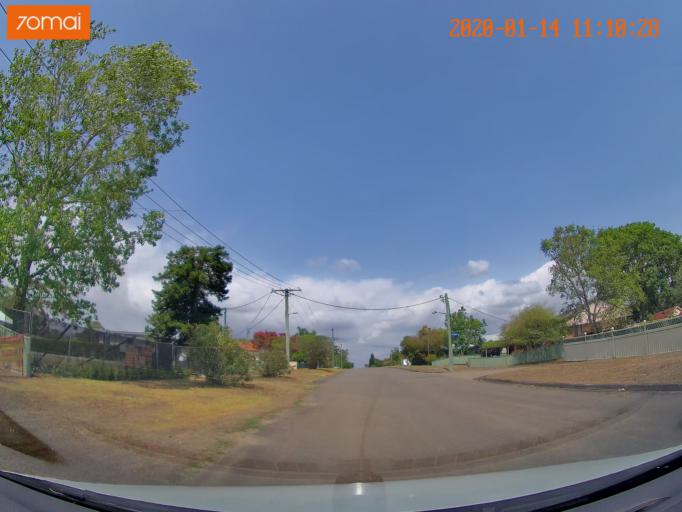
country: AU
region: New South Wales
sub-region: Lake Macquarie Shire
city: Dora Creek
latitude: -33.0957
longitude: 151.4776
